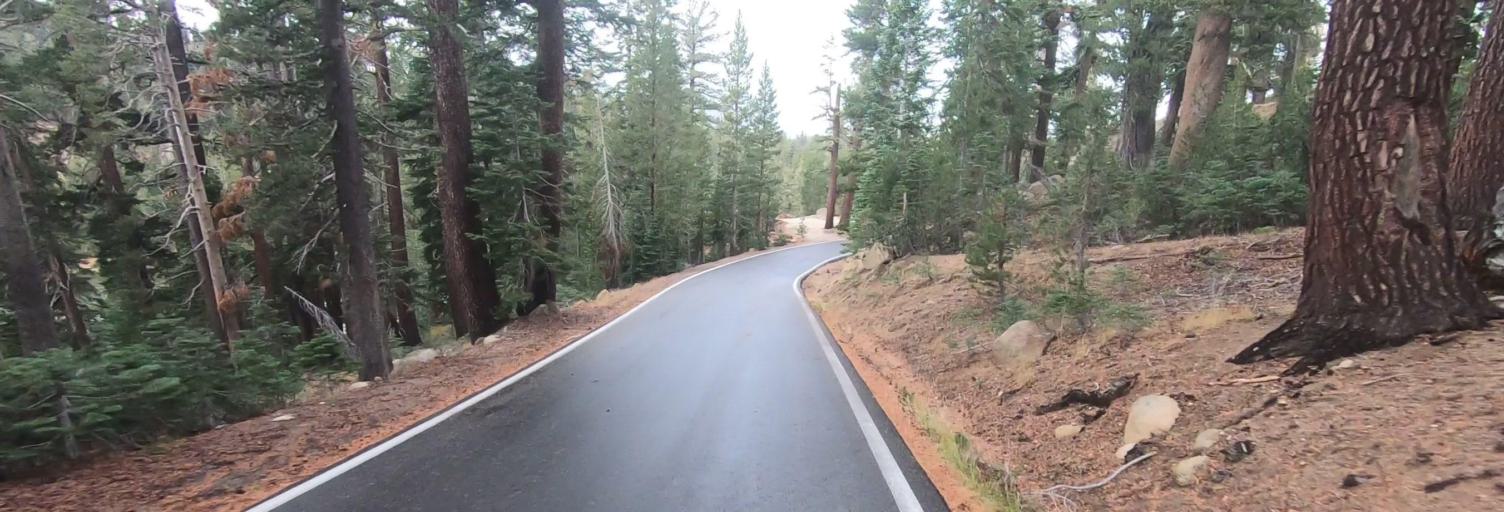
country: US
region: Nevada
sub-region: Douglas County
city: Gardnerville Ranchos
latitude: 38.5547
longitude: -119.8051
